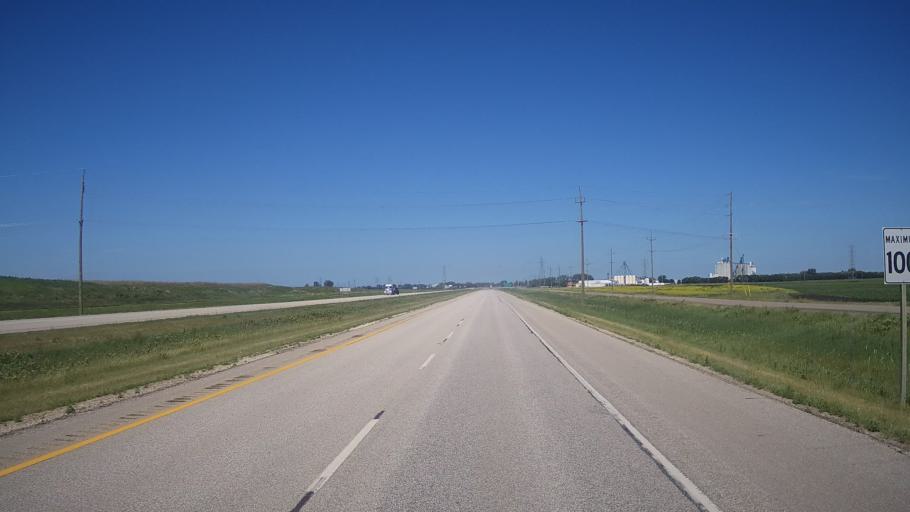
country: CA
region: Manitoba
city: Portage la Prairie
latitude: 49.9568
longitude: -98.3338
